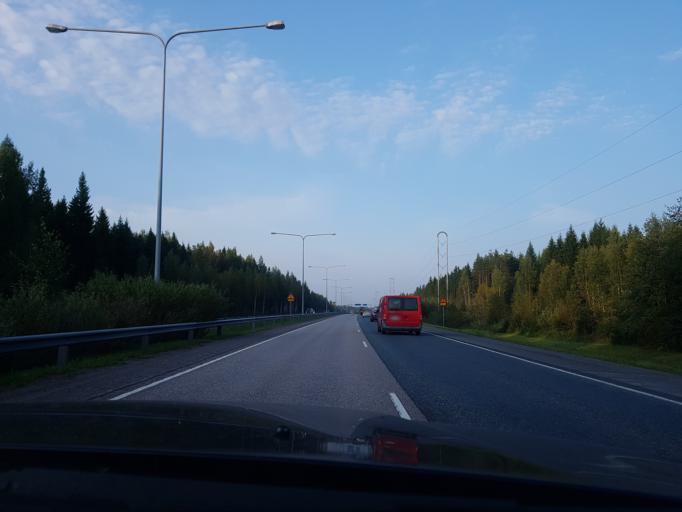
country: FI
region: Uusimaa
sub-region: Helsinki
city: Tuusula
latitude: 60.3620
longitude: 25.0030
